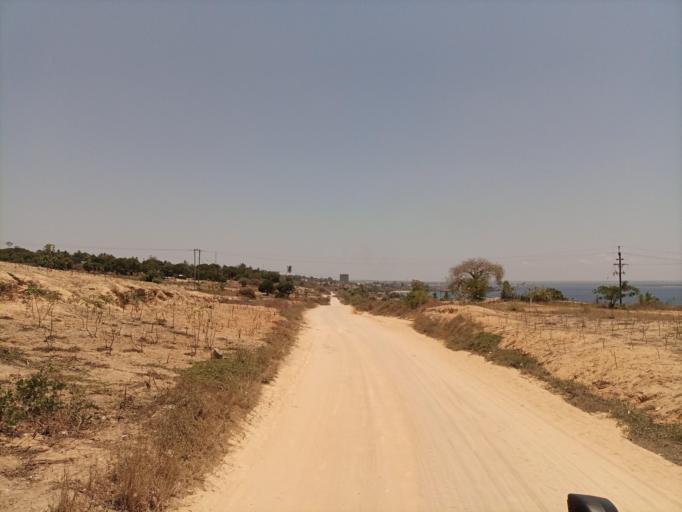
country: MZ
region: Nampula
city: Nacala
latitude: -14.5197
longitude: 40.6798
